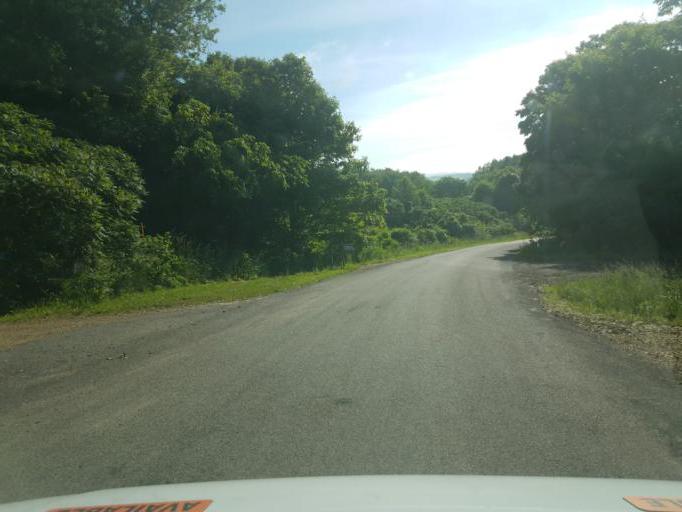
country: US
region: Wisconsin
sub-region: Sauk County
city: Reedsburg
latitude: 43.5801
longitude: -90.1530
